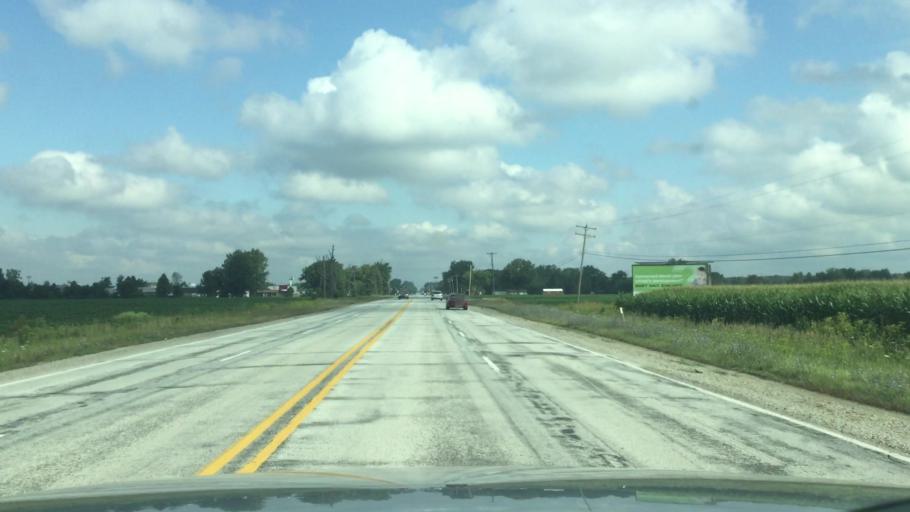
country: US
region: Michigan
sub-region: Saginaw County
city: Birch Run
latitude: 43.2397
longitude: -83.7614
